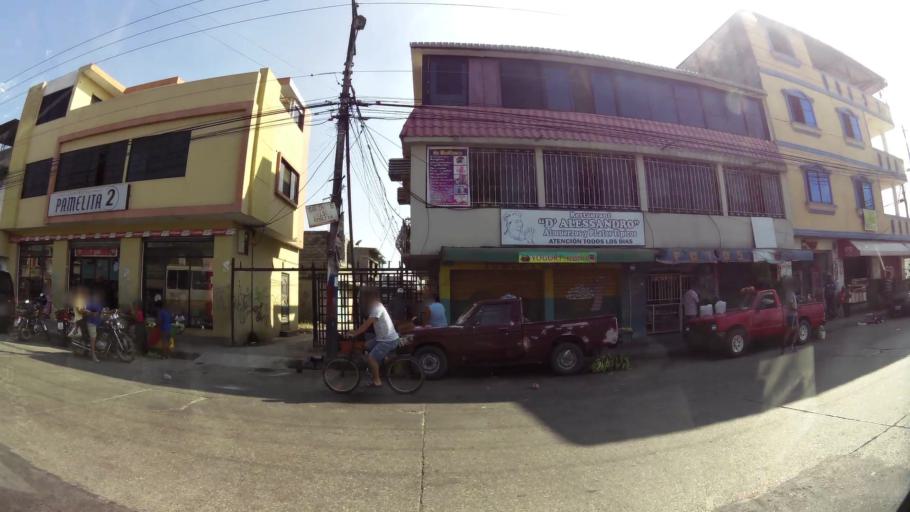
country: EC
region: Guayas
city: Eloy Alfaro
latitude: -2.1690
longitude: -79.8028
